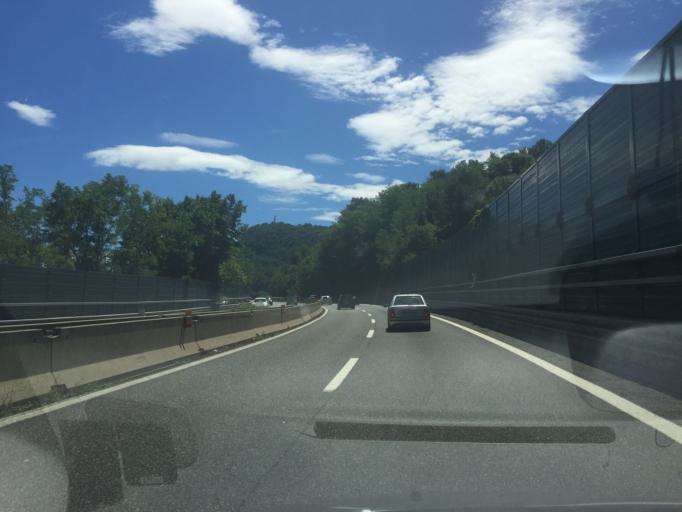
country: IT
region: Lombardy
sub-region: Provincia di Como
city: San Fermo della Battaglia
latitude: 45.8170
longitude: 9.0574
